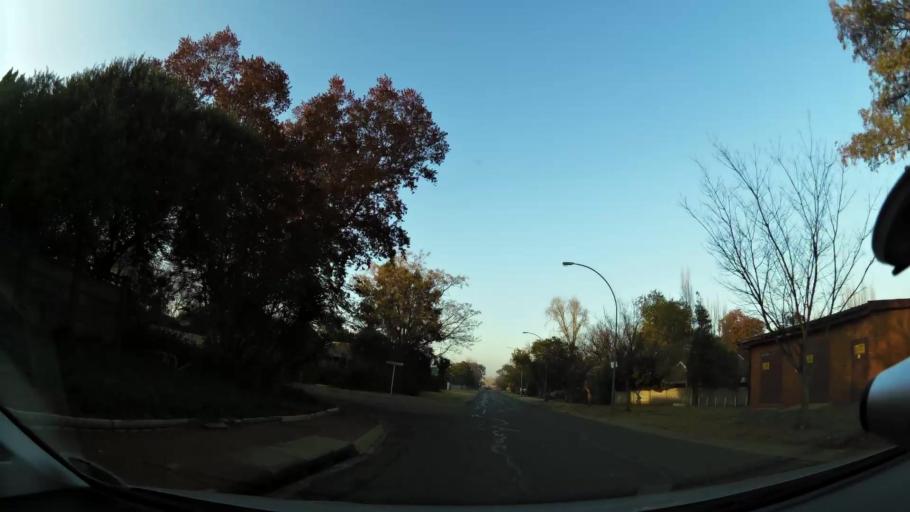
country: ZA
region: Orange Free State
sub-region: Mangaung Metropolitan Municipality
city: Bloemfontein
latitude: -29.1040
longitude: 26.1494
